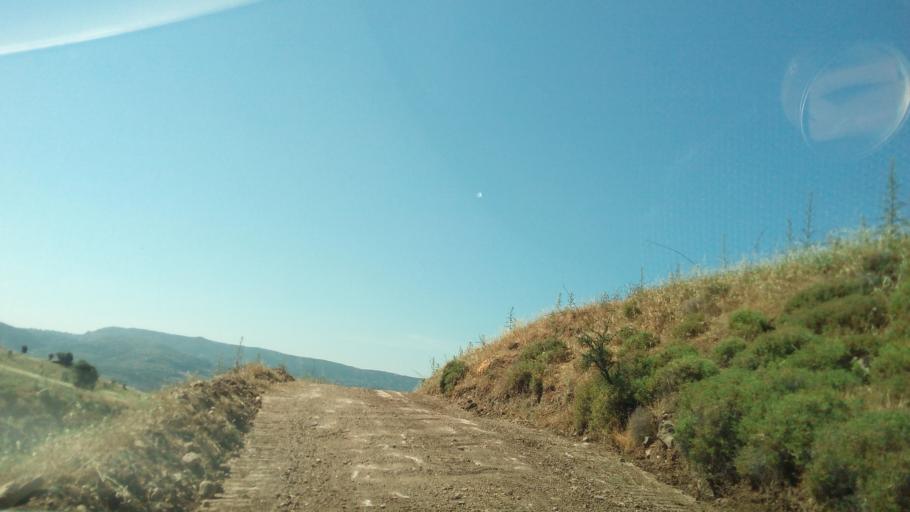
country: CY
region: Limassol
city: Pachna
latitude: 34.8227
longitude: 32.7021
